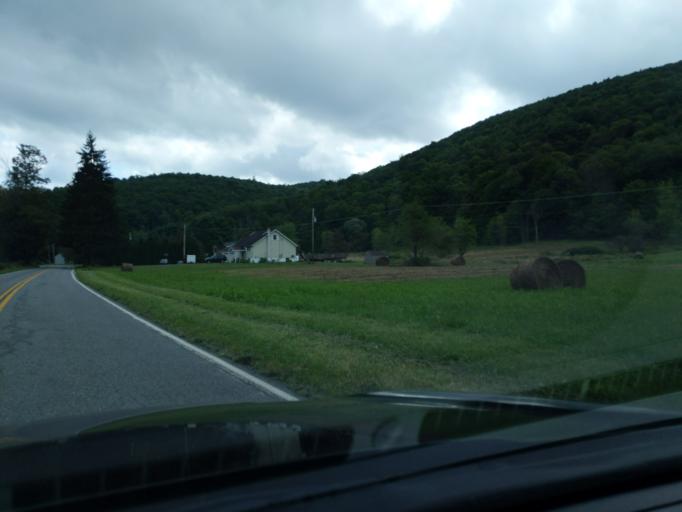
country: US
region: Pennsylvania
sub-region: Blair County
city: Duncansville
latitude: 40.3777
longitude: -78.4868
